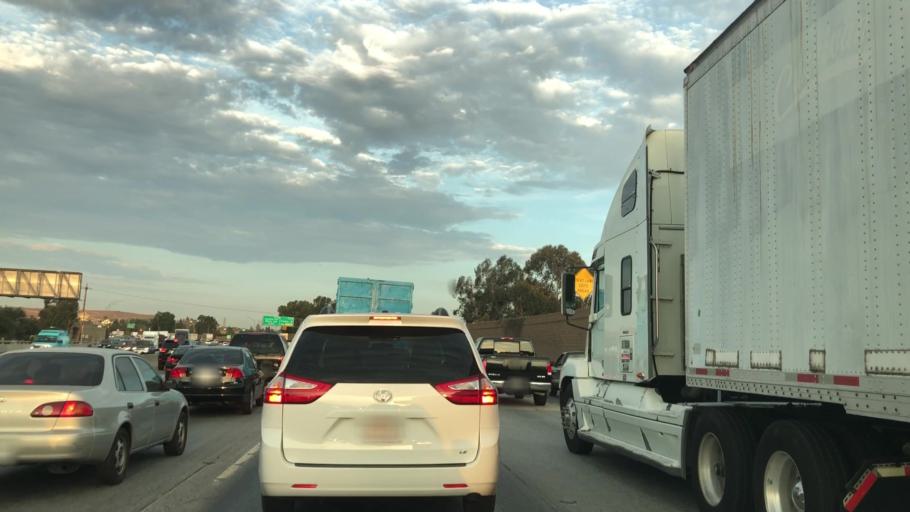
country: US
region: California
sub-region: Los Angeles County
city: Belvedere
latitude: 34.0334
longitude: -118.1466
